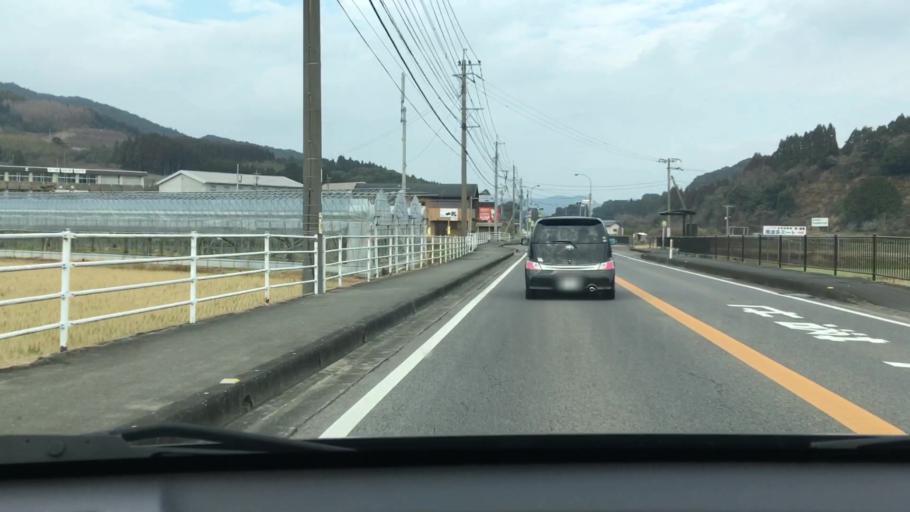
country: JP
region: Saga Prefecture
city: Imaricho-ko
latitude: 33.3158
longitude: 129.9288
